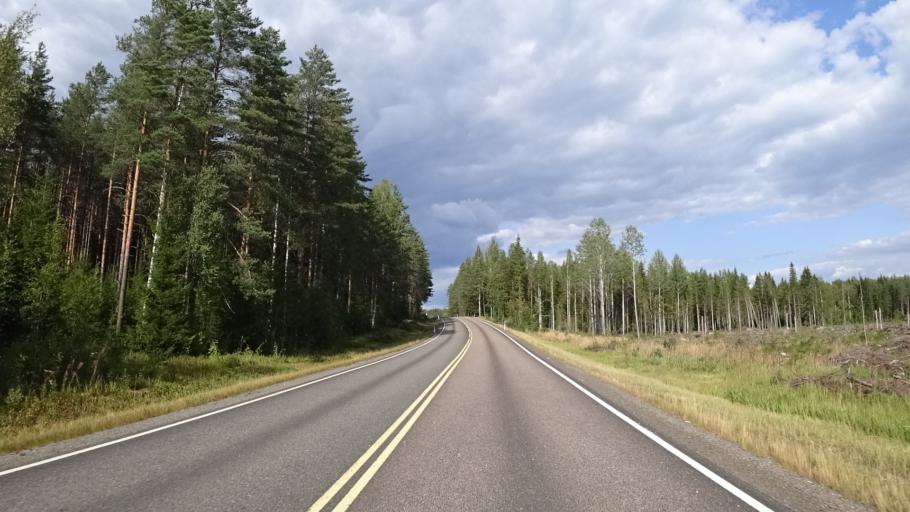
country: FI
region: South Karelia
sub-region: Lappeenranta
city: Taavetti
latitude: 60.8037
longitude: 27.3845
